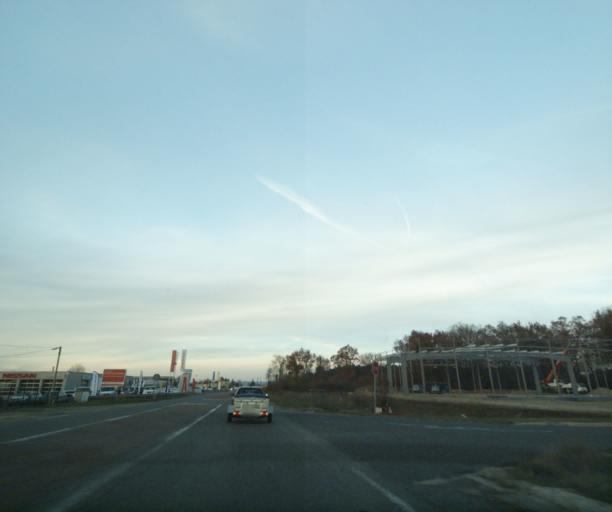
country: FR
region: Aquitaine
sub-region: Departement de la Gironde
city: Langon
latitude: 44.5221
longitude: -0.2401
